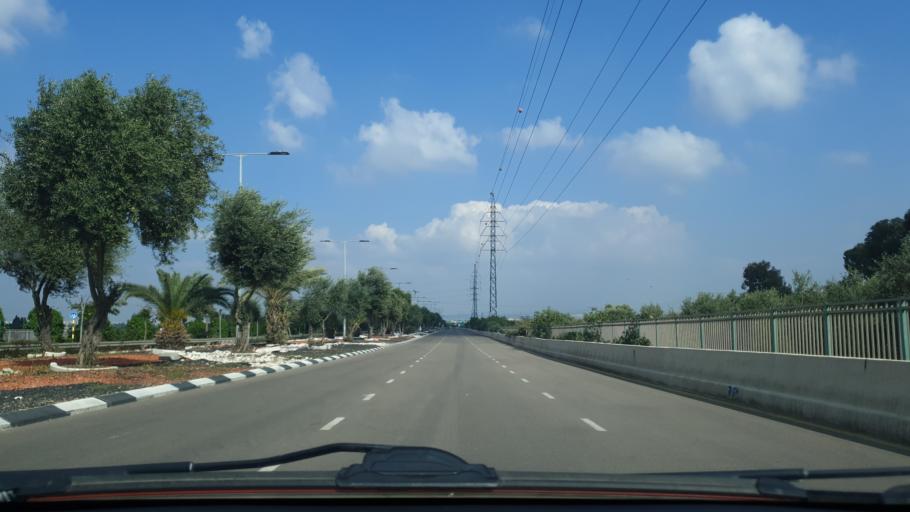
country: IL
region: Central District
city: Kefar Habad
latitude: 31.9713
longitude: 34.8344
